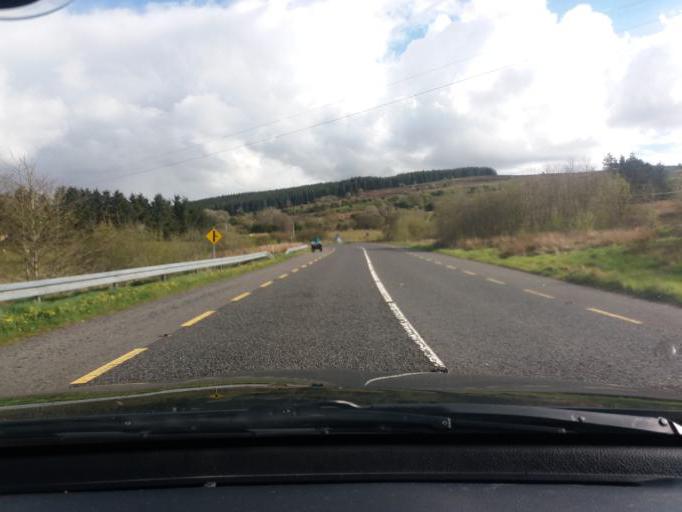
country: IE
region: Connaught
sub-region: County Leitrim
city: Manorhamilton
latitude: 54.3465
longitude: -8.2370
